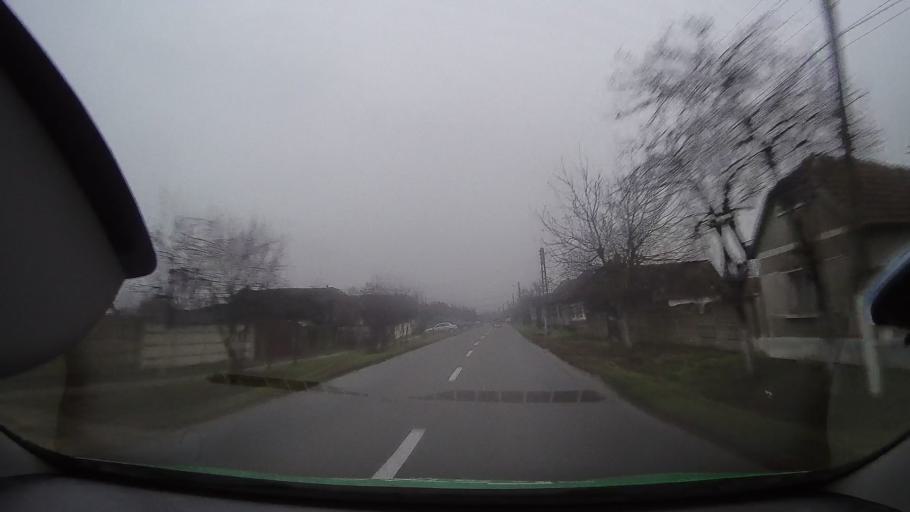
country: RO
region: Bihor
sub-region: Comuna Tulca
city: Tulca
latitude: 46.7880
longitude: 21.7786
